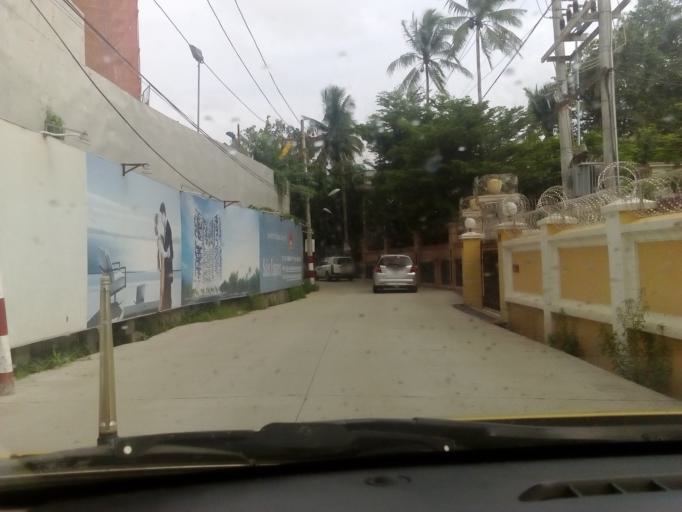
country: MM
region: Yangon
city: Yangon
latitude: 16.8500
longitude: 96.1507
